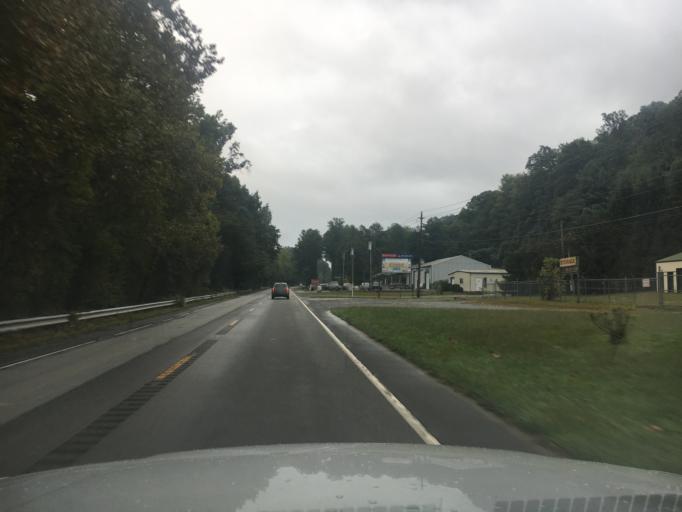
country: US
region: North Carolina
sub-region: Henderson County
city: Horse Shoe
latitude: 35.3353
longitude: -82.5681
